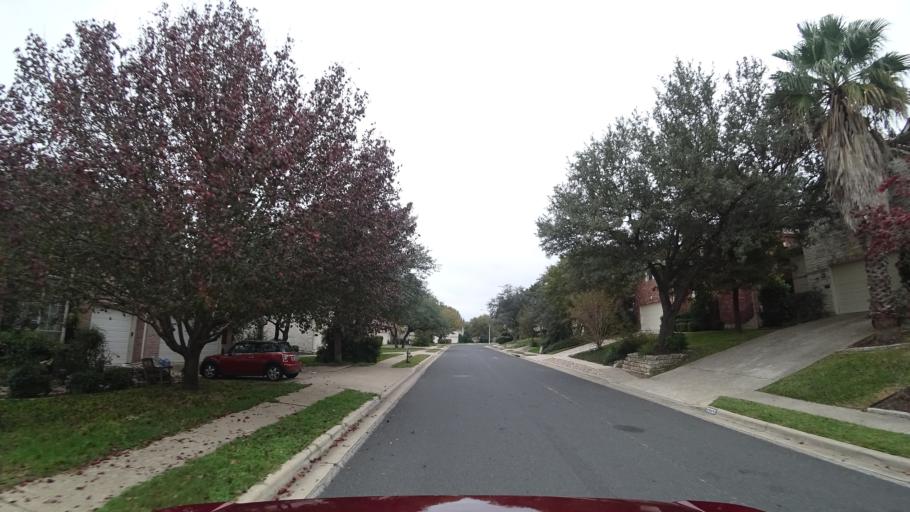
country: US
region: Texas
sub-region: Williamson County
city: Anderson Mill
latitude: 30.4360
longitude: -97.8160
